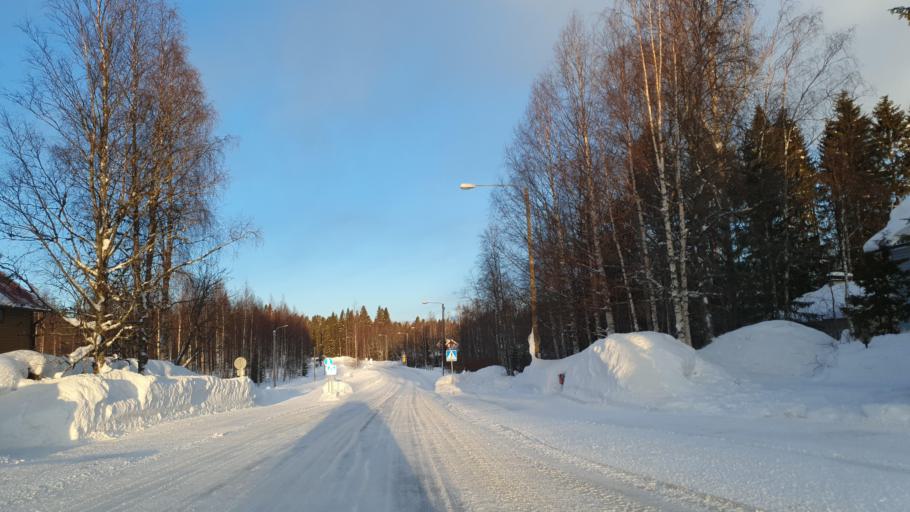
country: FI
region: Kainuu
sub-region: Kajaani
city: Ristijaervi
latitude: 64.3380
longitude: 28.1087
